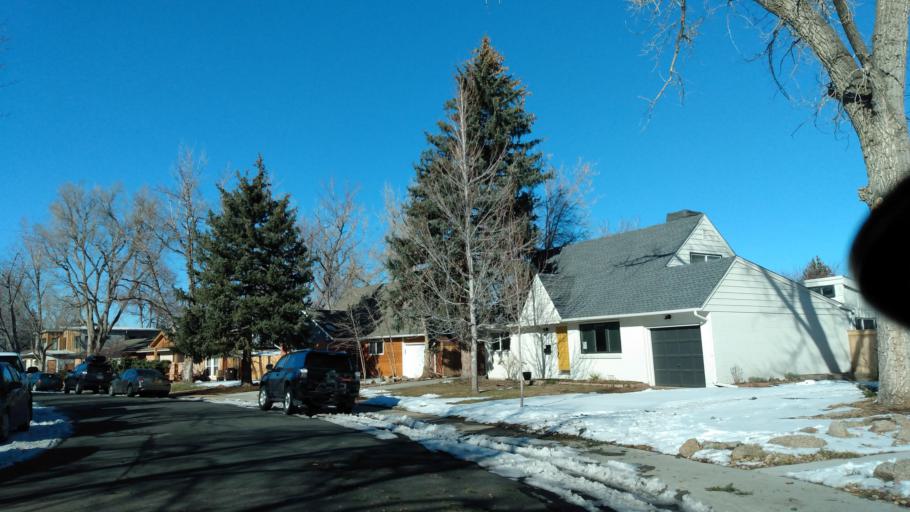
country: US
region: Colorado
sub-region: Boulder County
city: Boulder
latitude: 39.9870
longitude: -105.2417
